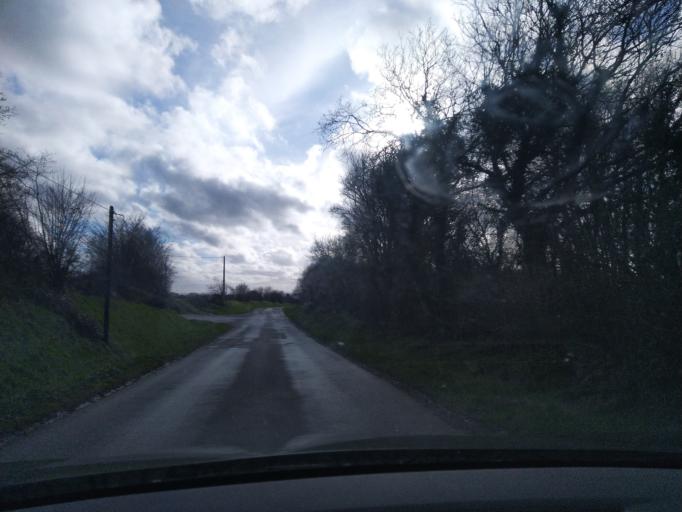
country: FR
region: Brittany
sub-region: Departement du Finistere
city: Guerlesquin
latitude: 48.4725
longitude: -3.5776
